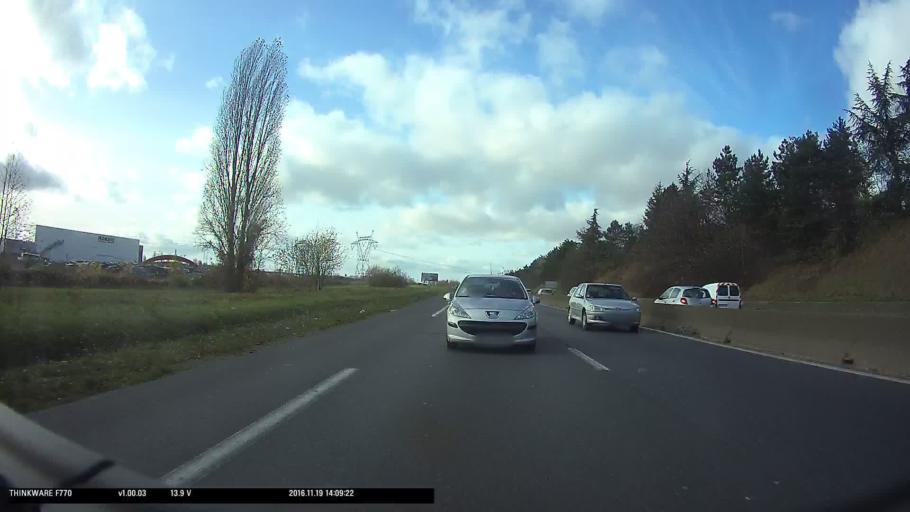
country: FR
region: Ile-de-France
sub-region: Departement du Val-d'Oise
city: Osny
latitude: 49.0544
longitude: 2.0566
